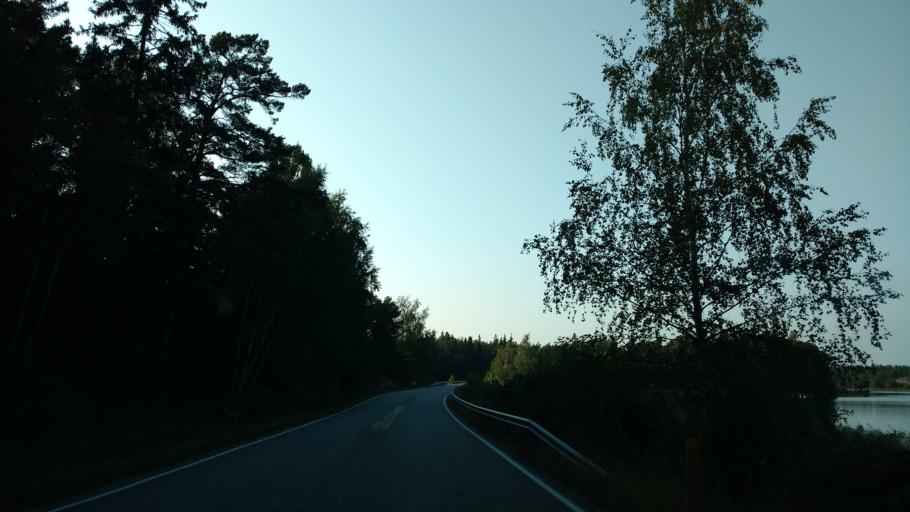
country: FI
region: Varsinais-Suomi
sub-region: Aboland-Turunmaa
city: Dragsfjaerd
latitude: 59.9956
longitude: 22.4536
